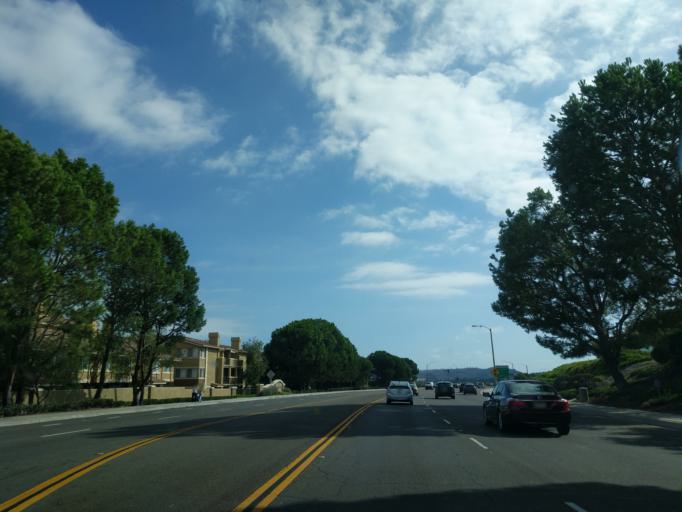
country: US
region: California
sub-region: Orange County
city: Aliso Viejo
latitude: 33.5839
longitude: -117.7195
